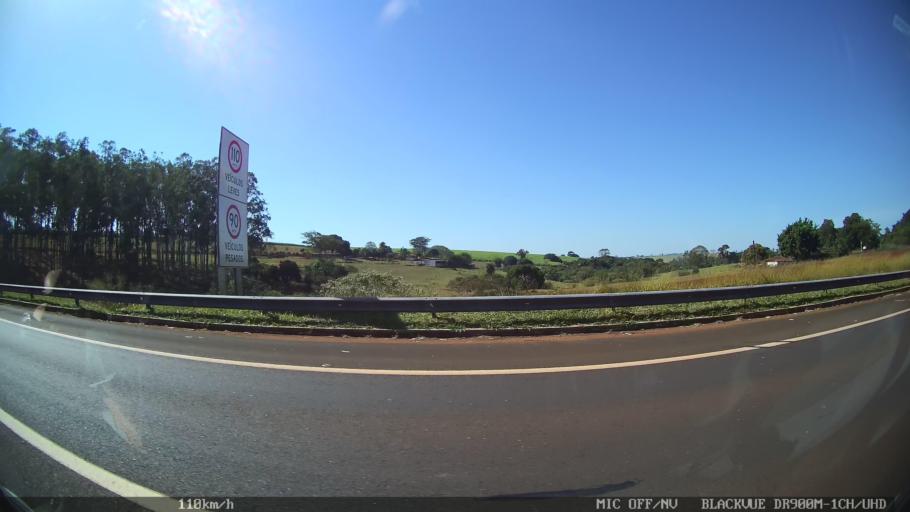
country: BR
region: Sao Paulo
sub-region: Batatais
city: Batatais
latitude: -20.8453
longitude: -47.6013
